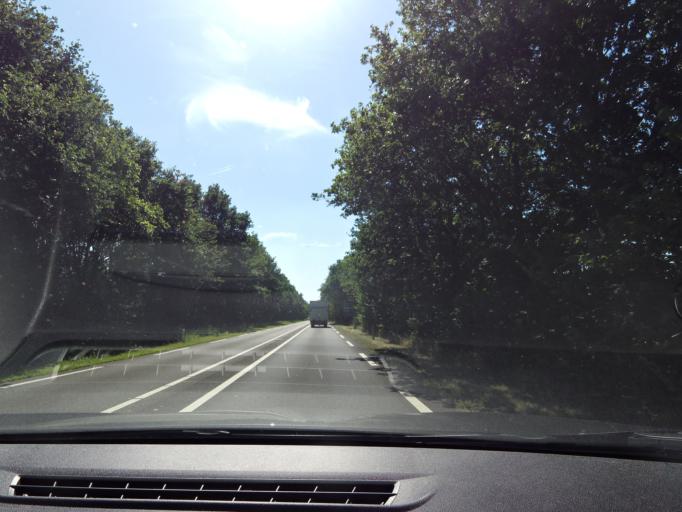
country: NL
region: Gelderland
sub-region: Oost Gelre
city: Lichtenvoorde
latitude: 52.0079
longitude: 6.6017
